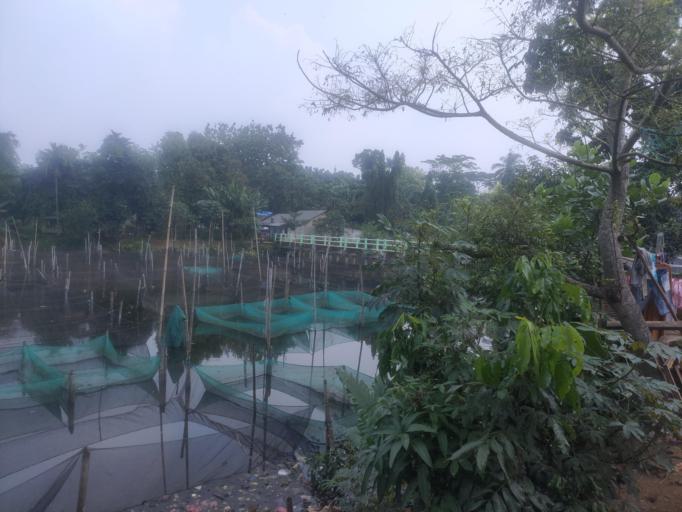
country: ID
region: West Java
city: Parung
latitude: -6.4458
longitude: 106.6939
